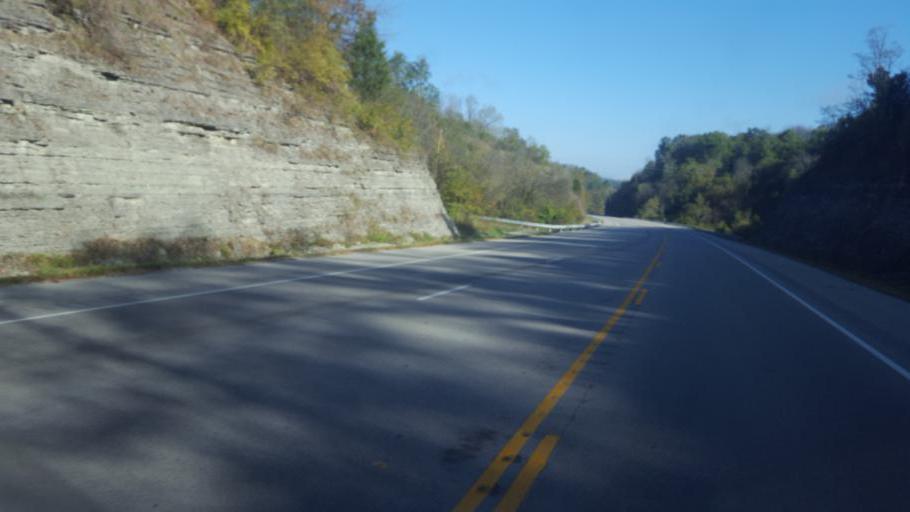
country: US
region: Kentucky
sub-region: Mason County
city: Maysville
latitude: 38.6081
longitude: -83.7574
